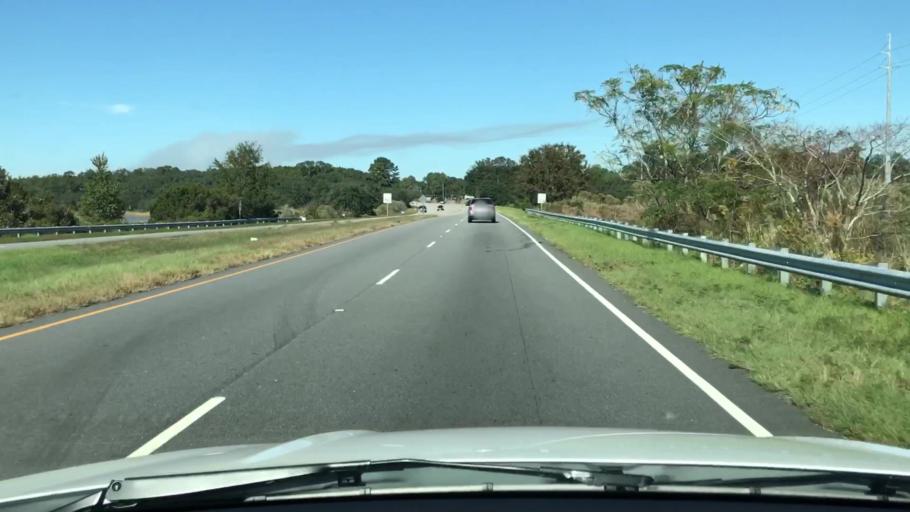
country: US
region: South Carolina
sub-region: Beaufort County
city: Laurel Bay
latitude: 32.5436
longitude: -80.7445
